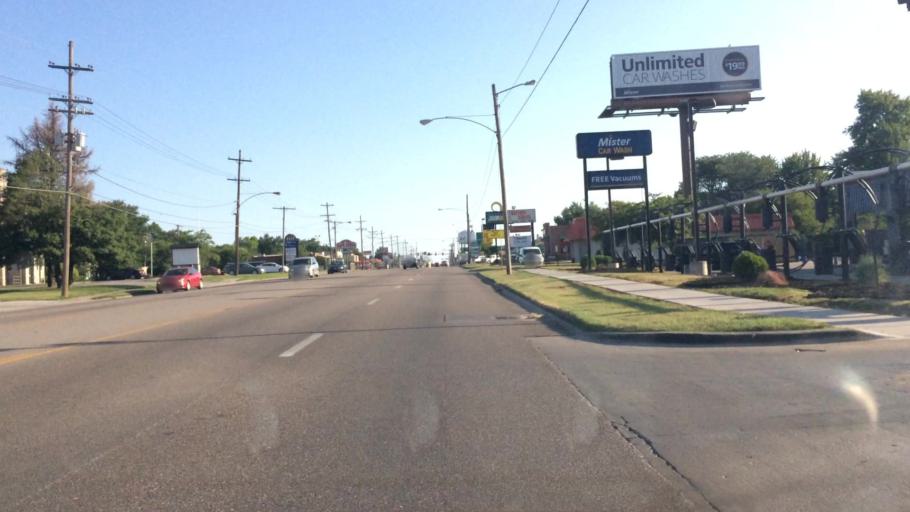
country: US
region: Missouri
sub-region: Greene County
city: Springfield
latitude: 37.1930
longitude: -93.2621
